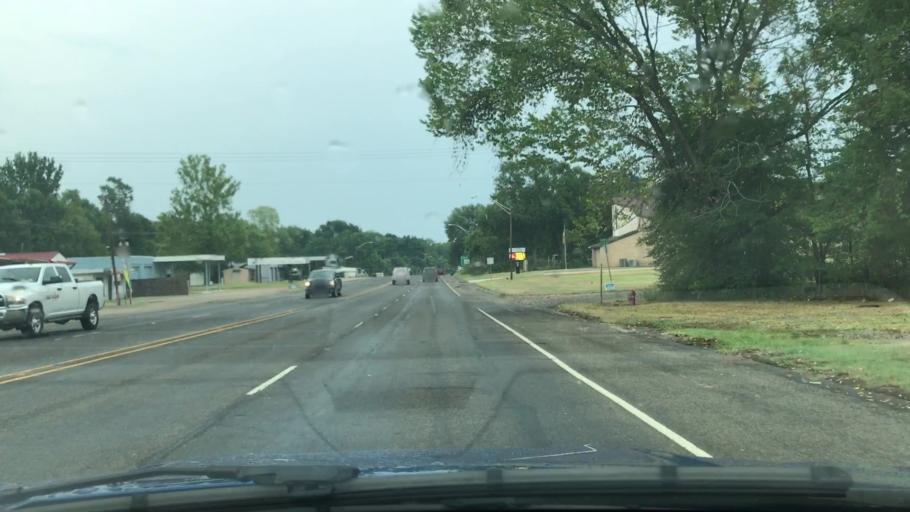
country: US
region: Texas
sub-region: Harrison County
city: Waskom
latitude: 32.4783
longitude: -94.0570
